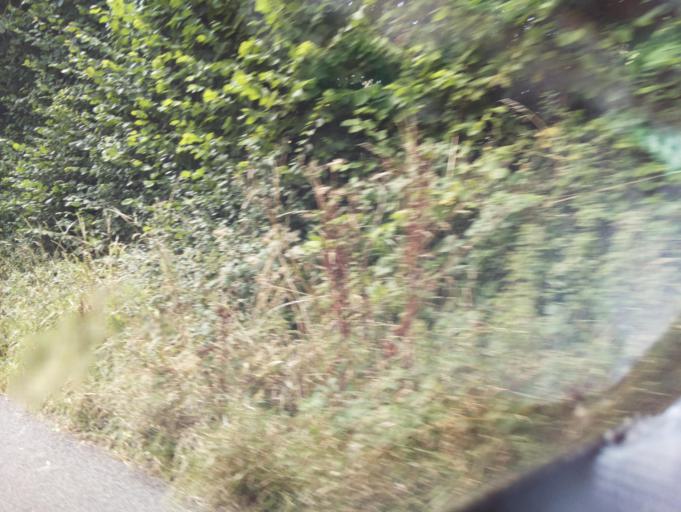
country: GB
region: England
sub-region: Devon
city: Dartmouth
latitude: 50.3610
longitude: -3.5616
